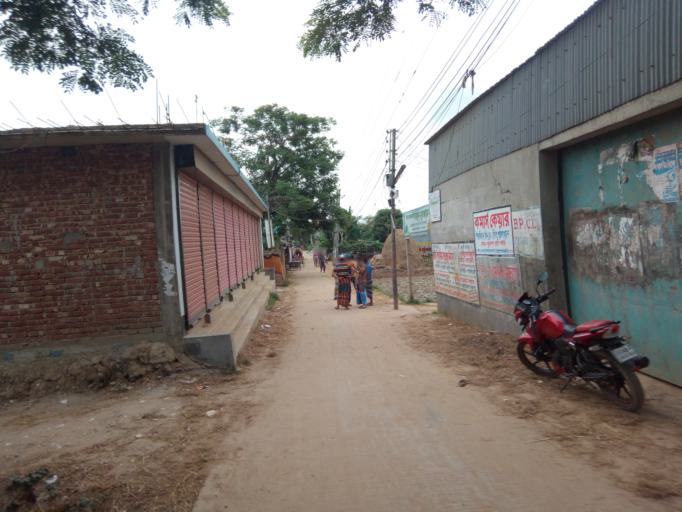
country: BD
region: Dhaka
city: Paltan
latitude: 23.7376
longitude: 90.4526
